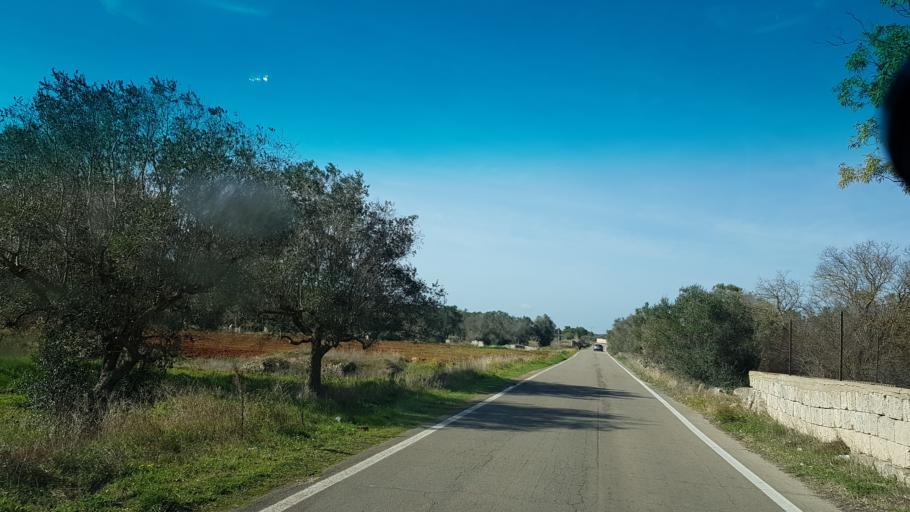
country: IT
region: Apulia
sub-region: Provincia di Lecce
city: Arnesano
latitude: 40.3511
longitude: 18.1073
